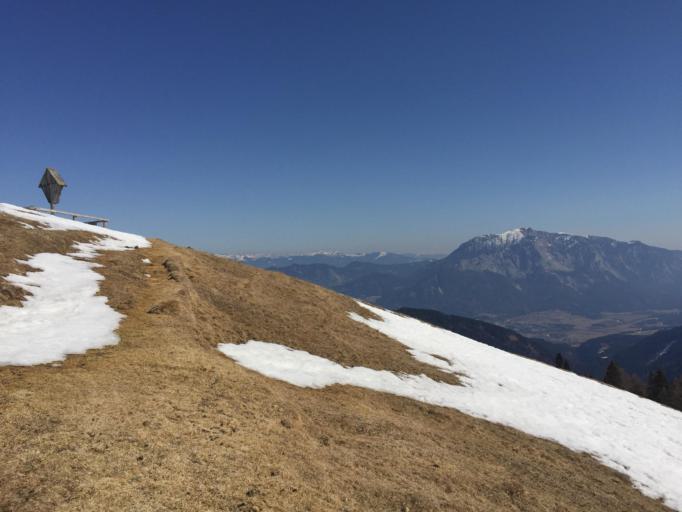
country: IT
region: Friuli Venezia Giulia
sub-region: Provincia di Udine
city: Tarvisio
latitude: 46.5485
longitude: 13.5164
